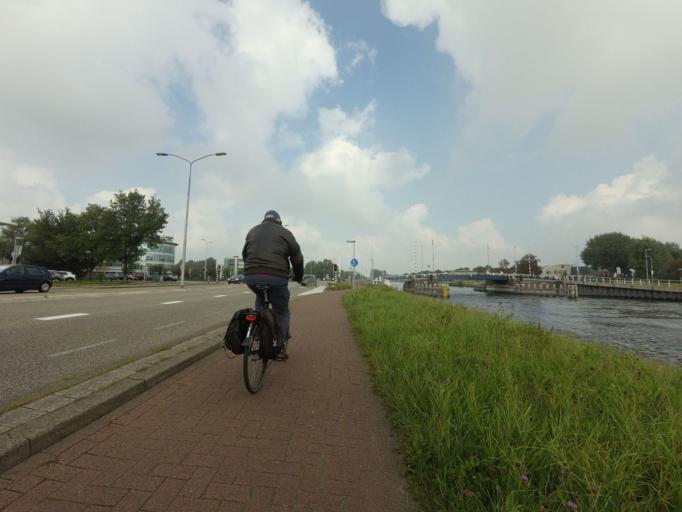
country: NL
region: North Holland
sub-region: Gemeente Alkmaar
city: Alkmaar
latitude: 52.6484
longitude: 4.7430
